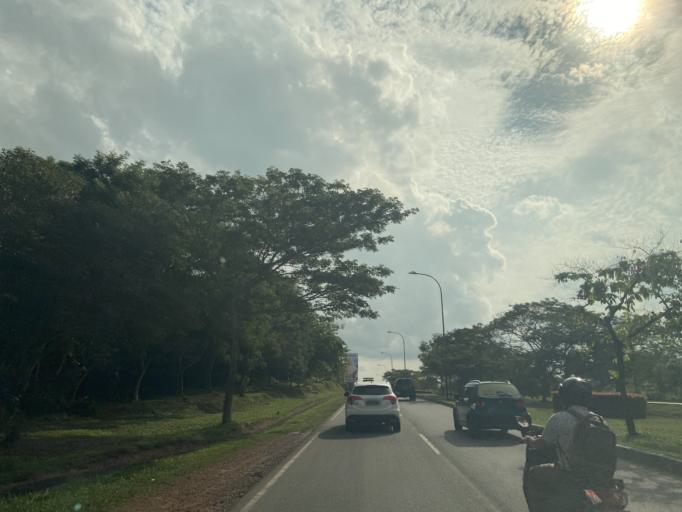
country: SG
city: Singapore
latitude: 1.0998
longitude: 104.0738
